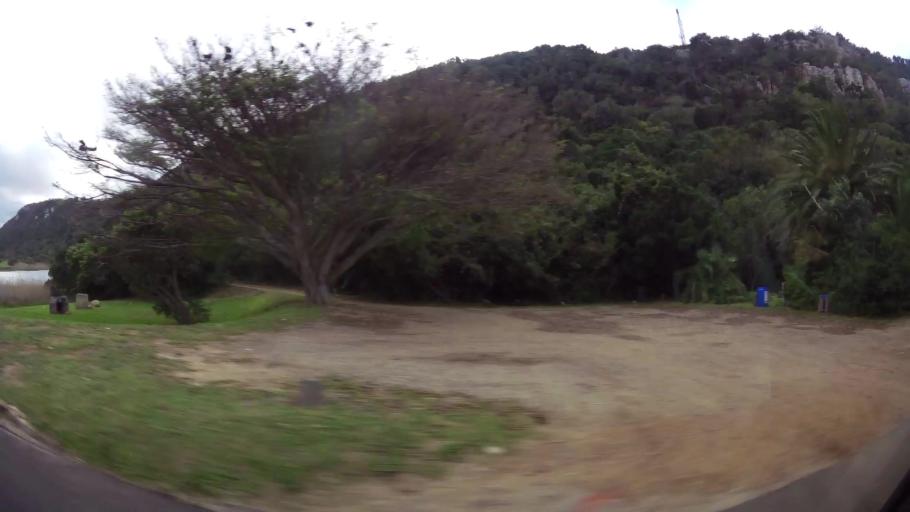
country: ZA
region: Western Cape
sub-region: Eden District Municipality
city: Plettenberg Bay
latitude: -34.0606
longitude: 23.3731
